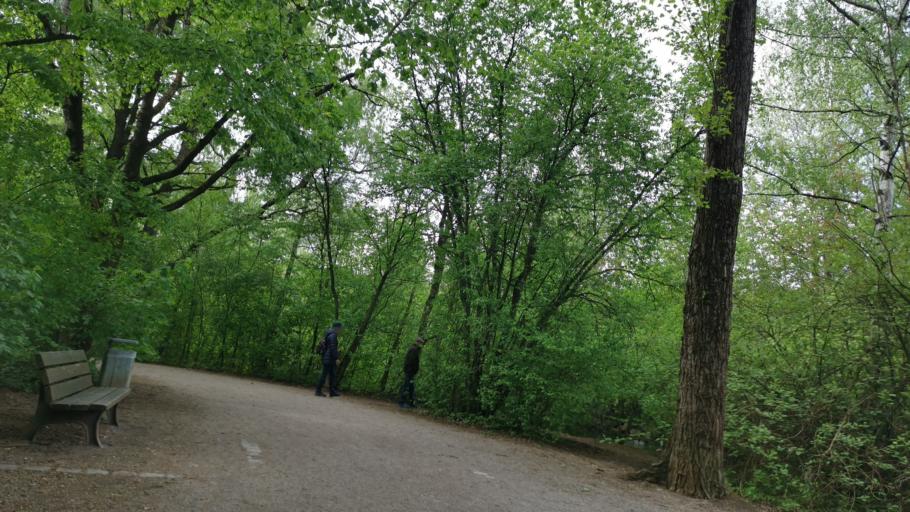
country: DE
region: Bavaria
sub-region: Upper Bavaria
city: Bogenhausen
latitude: 48.1718
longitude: 11.5906
